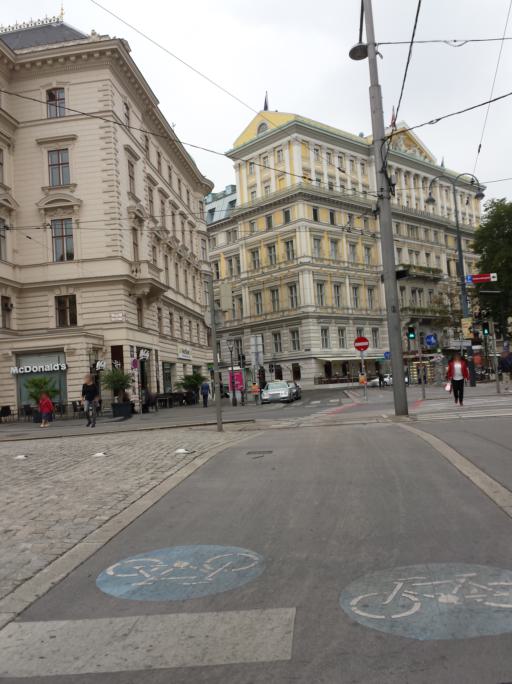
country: AT
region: Vienna
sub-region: Wien Stadt
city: Vienna
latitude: 48.2015
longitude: 16.3746
